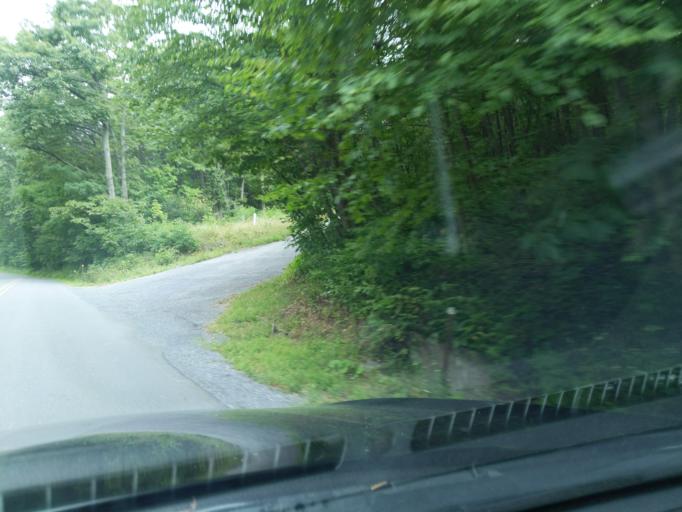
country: US
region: Pennsylvania
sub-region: Blair County
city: Claysburg
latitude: 40.2904
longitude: -78.5712
